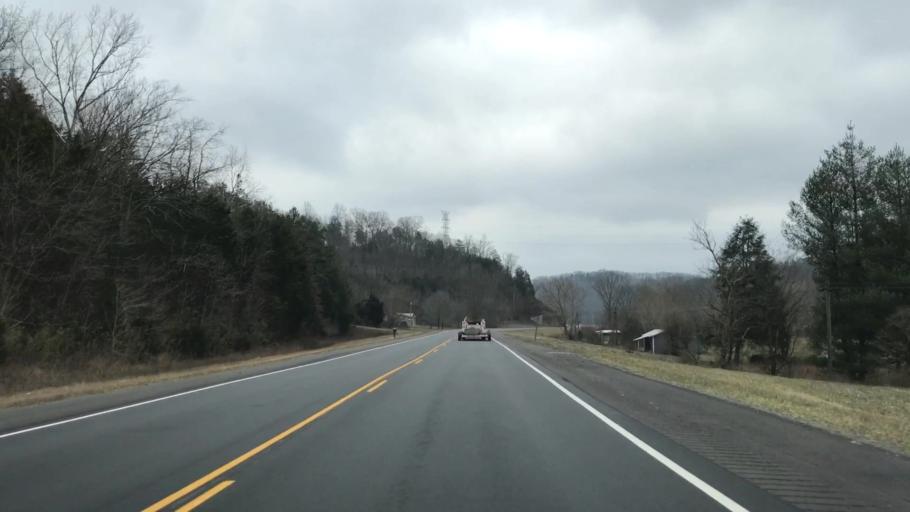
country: US
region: Kentucky
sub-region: Cumberland County
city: Burkesville
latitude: 36.8938
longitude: -85.4263
